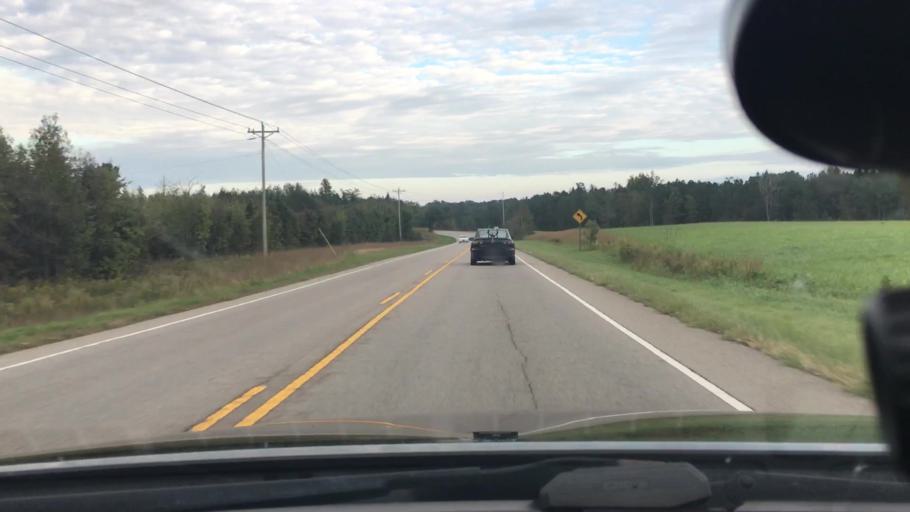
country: US
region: North Carolina
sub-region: Moore County
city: Robbins
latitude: 35.3997
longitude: -79.5505
